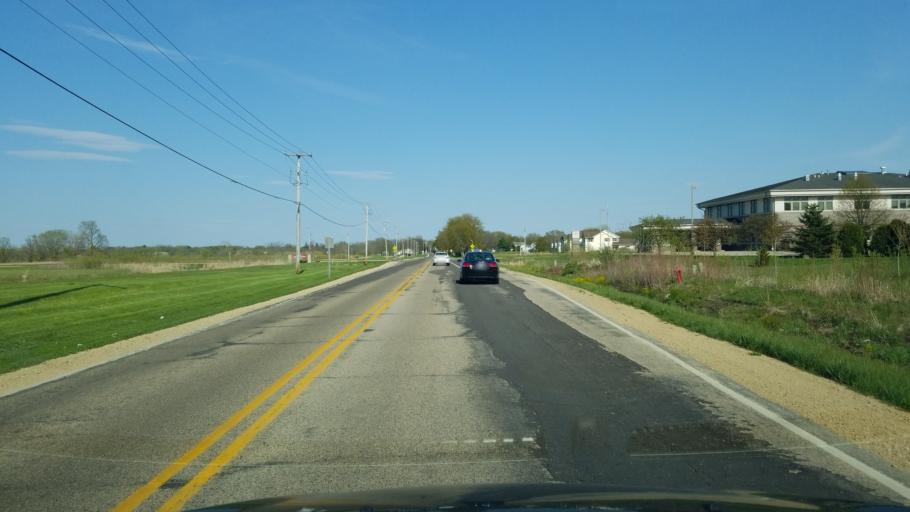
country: US
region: Wisconsin
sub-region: Dane County
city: Oregon
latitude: 42.9289
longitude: -89.4022
